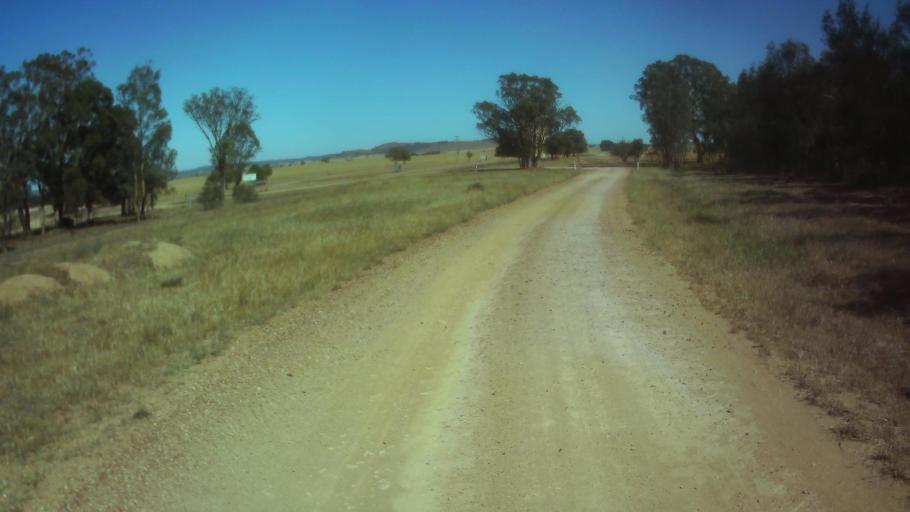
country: AU
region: New South Wales
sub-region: Weddin
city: Grenfell
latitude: -33.9917
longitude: 148.3409
